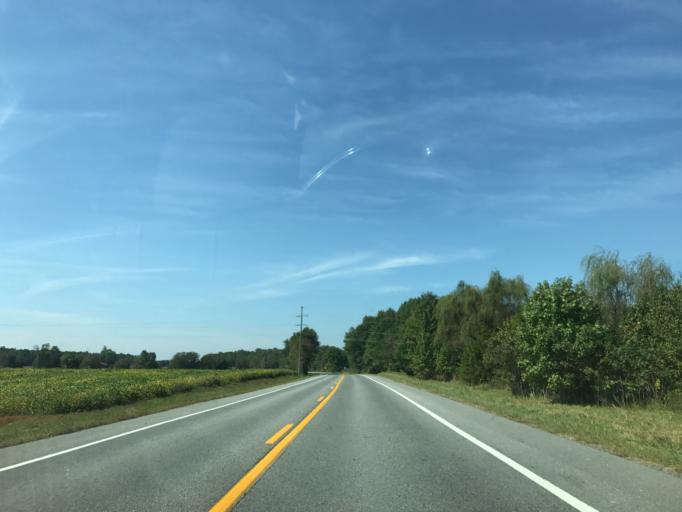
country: US
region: Delaware
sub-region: New Castle County
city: Townsend
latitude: 39.3015
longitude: -75.7619
